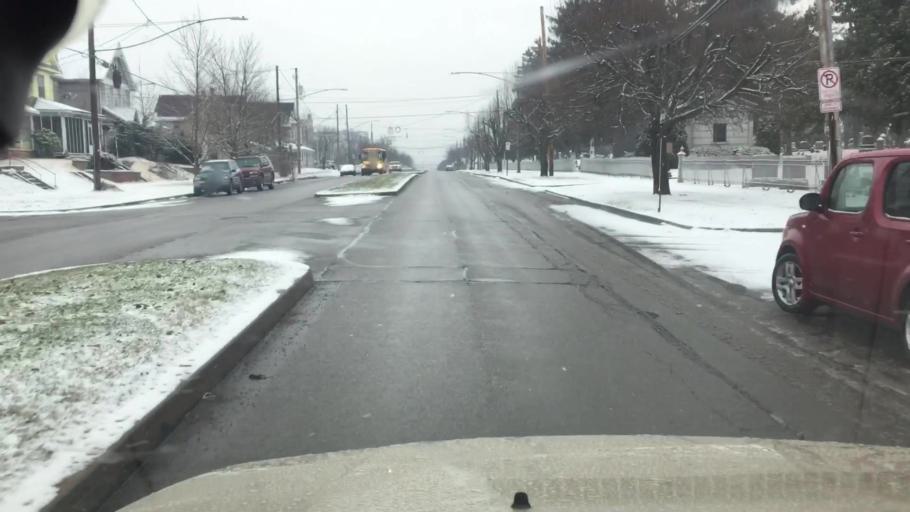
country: US
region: Pennsylvania
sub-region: Columbia County
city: Berwick
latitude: 41.0594
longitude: -76.2376
